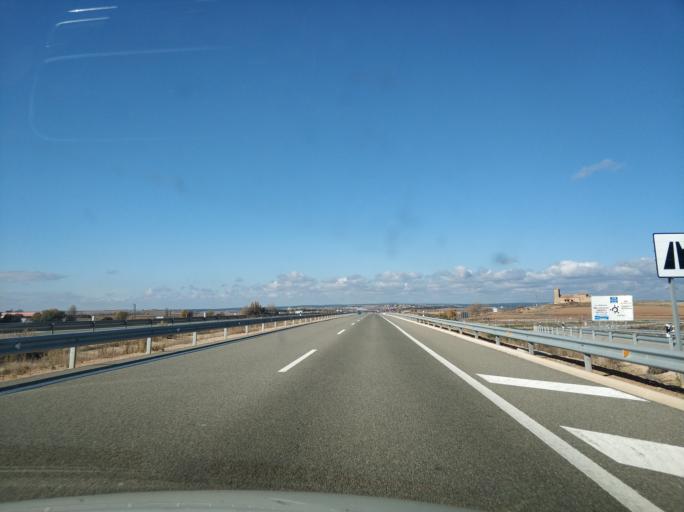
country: ES
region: Castille and Leon
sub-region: Provincia de Soria
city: Frechilla de Almazan
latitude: 41.4450
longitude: -2.5054
